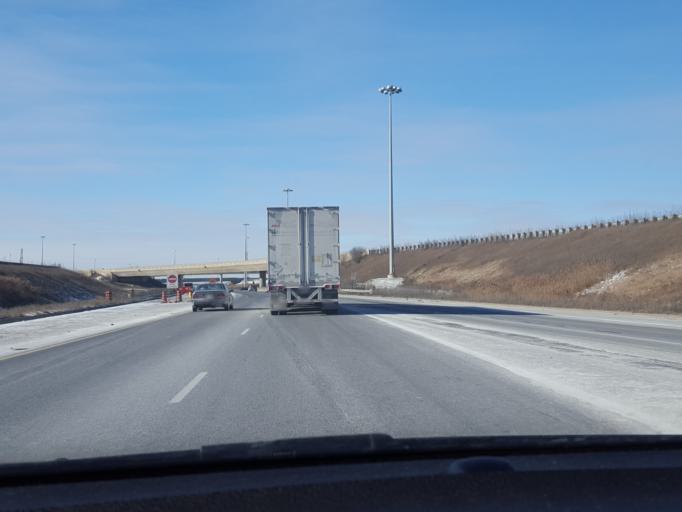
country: CA
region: Ontario
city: Mississauga
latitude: 43.6438
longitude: -79.6511
